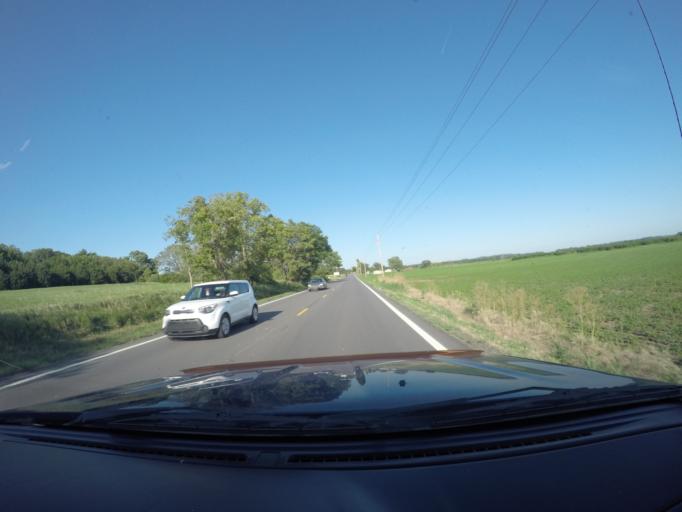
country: US
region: Kansas
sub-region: Douglas County
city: Lawrence
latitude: 39.0655
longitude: -95.3135
